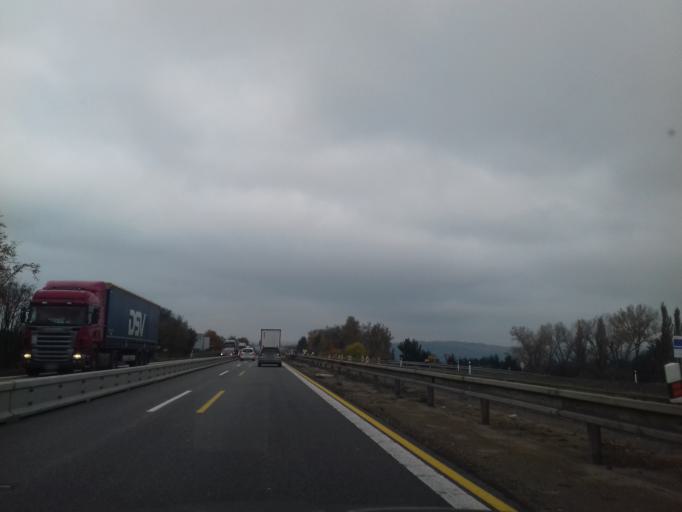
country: CZ
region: Central Bohemia
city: Trhovy Stepanov
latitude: 49.7251
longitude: 15.0480
